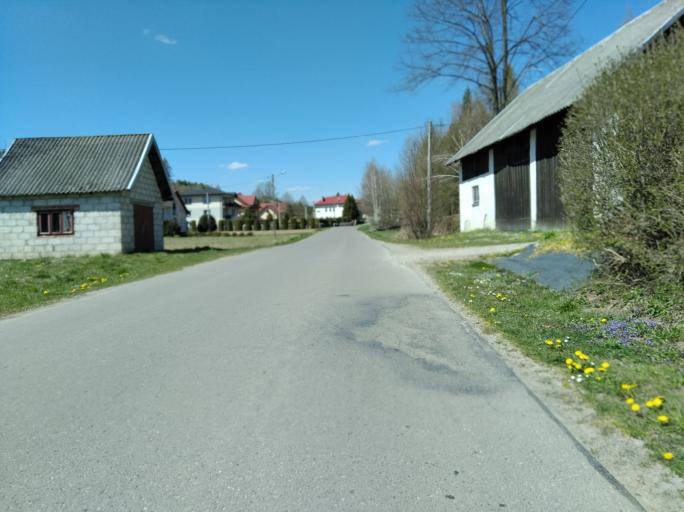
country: PL
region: Subcarpathian Voivodeship
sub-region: Powiat brzozowski
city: Jablonka
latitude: 49.7132
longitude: 22.1376
